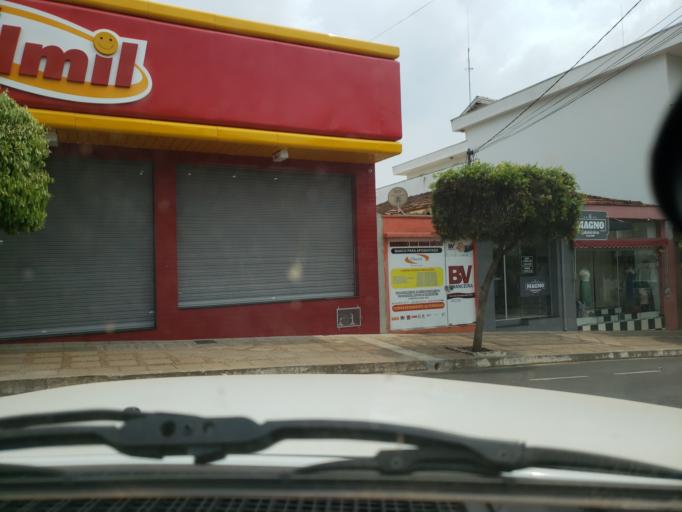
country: BR
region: Minas Gerais
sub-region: Jacutinga
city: Jacutinga
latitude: -22.2901
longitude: -46.6133
